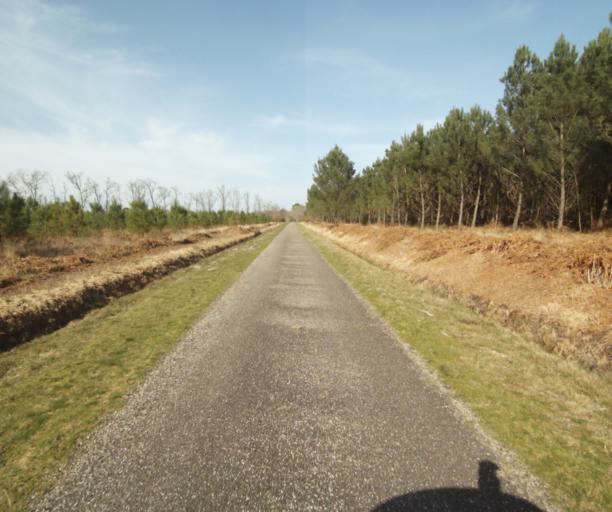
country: FR
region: Aquitaine
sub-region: Departement des Landes
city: Roquefort
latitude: 44.1441
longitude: -0.2046
